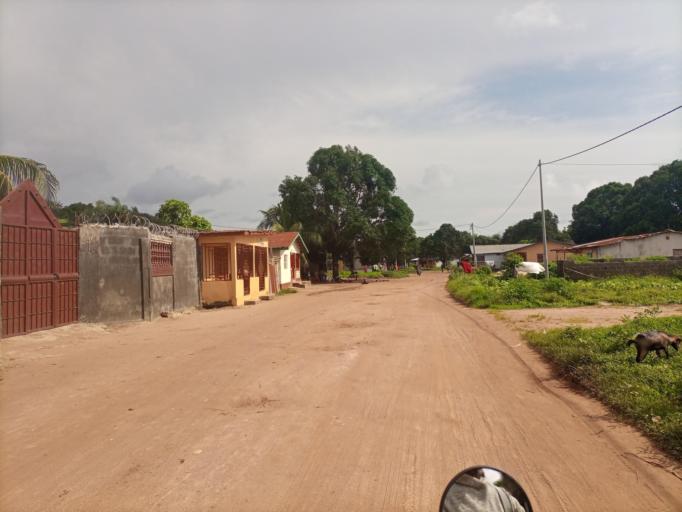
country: SL
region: Northern Province
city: Masoyila
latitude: 8.6068
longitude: -13.1749
